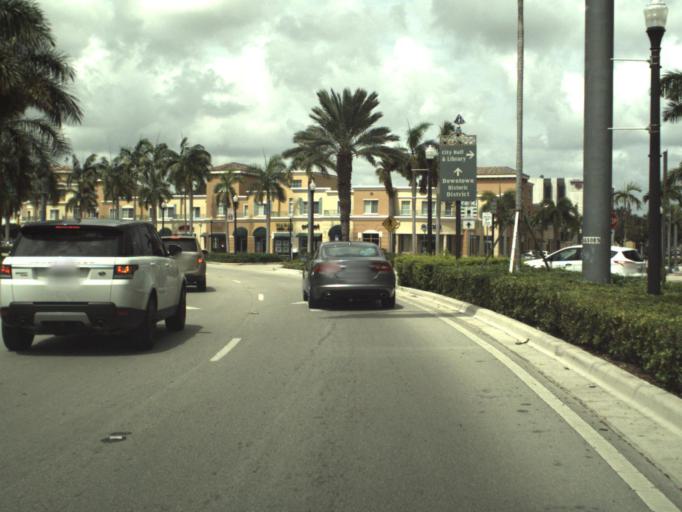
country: US
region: Florida
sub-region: Broward County
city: Hollywood
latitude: 26.0126
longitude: -80.1434
